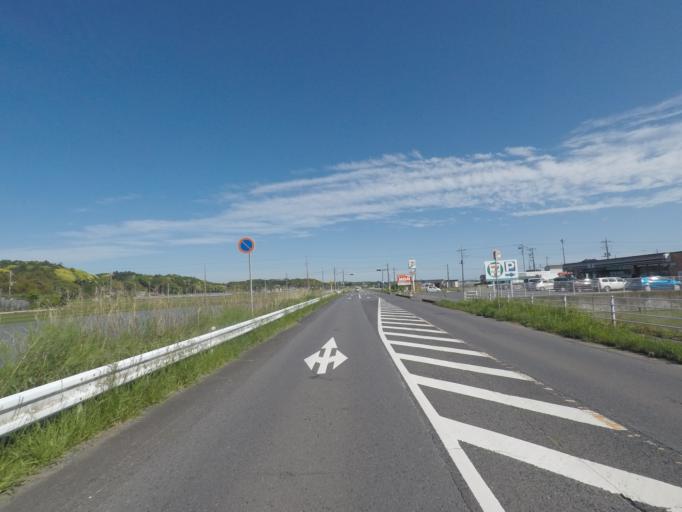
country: JP
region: Ibaraki
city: Inashiki
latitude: 36.0538
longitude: 140.4396
